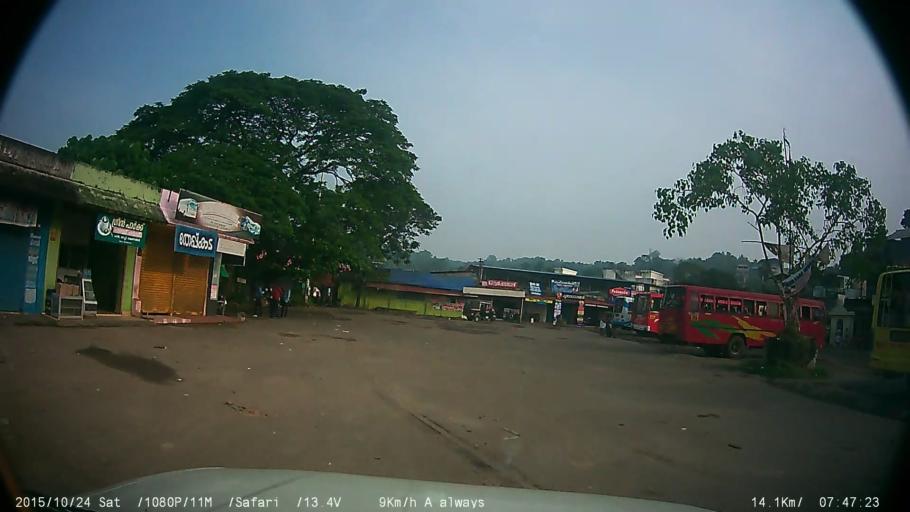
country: IN
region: Kerala
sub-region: Ernakulam
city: Piravam
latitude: 9.8631
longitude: 76.5934
